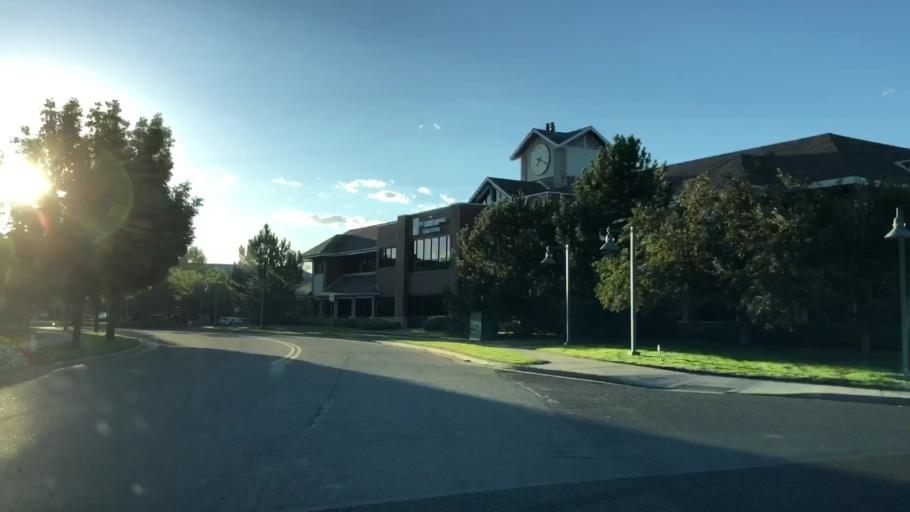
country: US
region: Colorado
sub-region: Larimer County
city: Loveland
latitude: 40.4091
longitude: -105.0002
